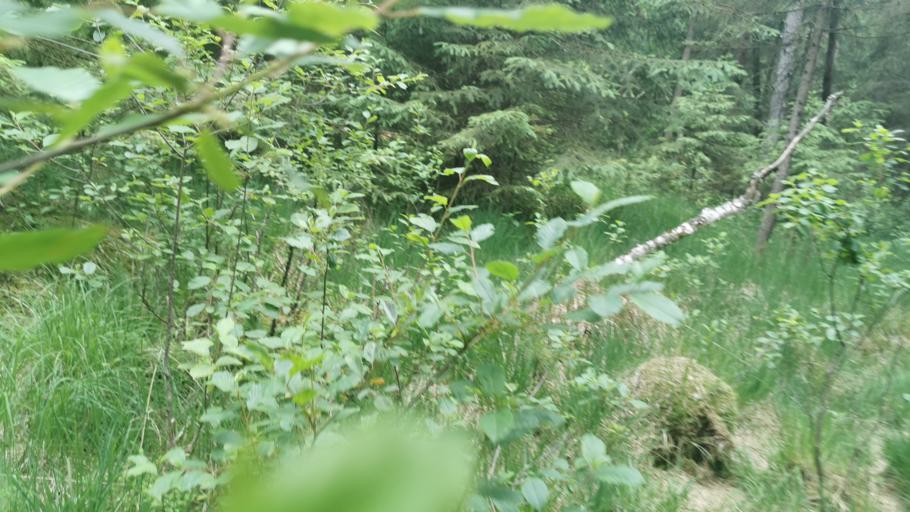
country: DE
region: Bavaria
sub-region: Upper Bavaria
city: Ainring
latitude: 47.7684
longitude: 12.9833
